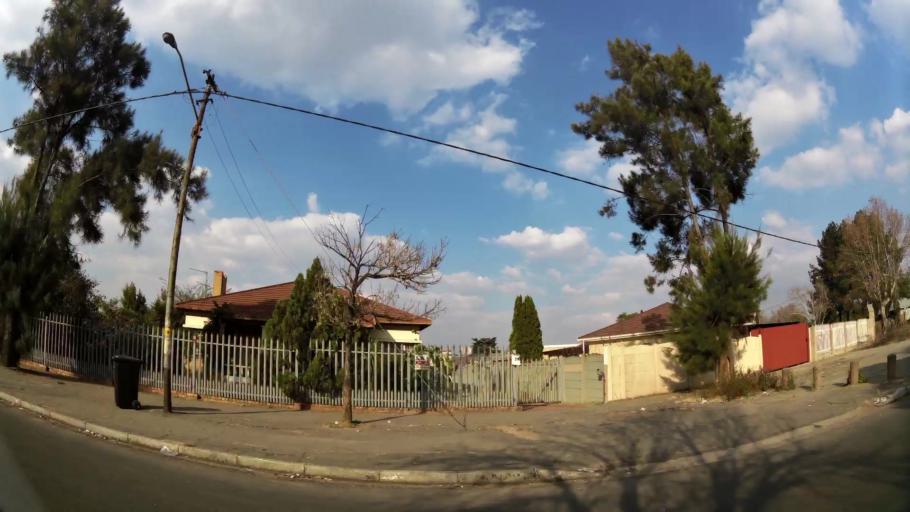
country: ZA
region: Gauteng
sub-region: Ekurhuleni Metropolitan Municipality
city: Germiston
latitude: -26.2295
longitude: 28.1824
